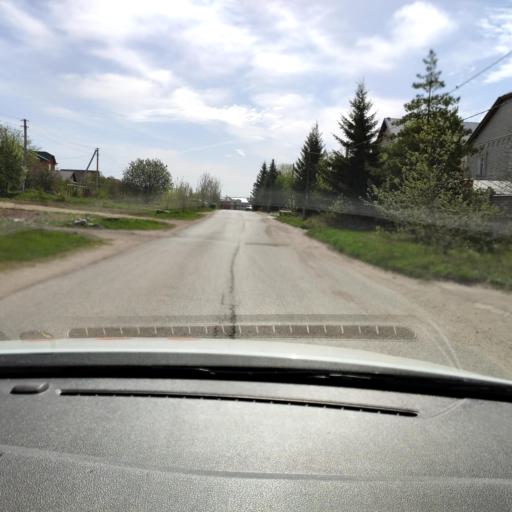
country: RU
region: Tatarstan
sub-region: Gorod Kazan'
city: Kazan
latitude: 55.8044
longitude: 49.2405
